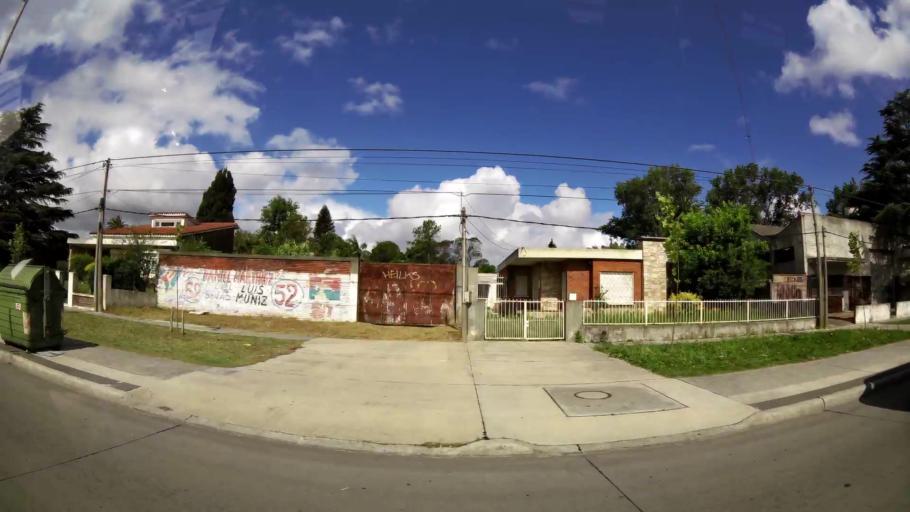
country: UY
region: Canelones
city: La Paz
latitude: -34.8325
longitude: -56.2211
